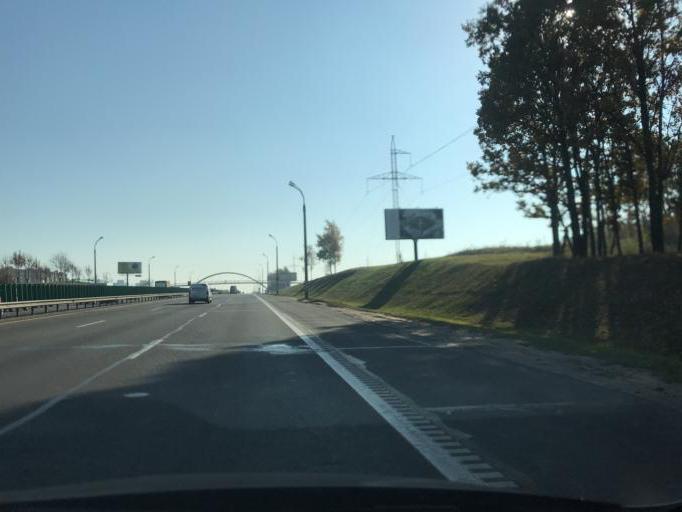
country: BY
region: Minsk
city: Malinovka
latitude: 53.8672
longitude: 27.4239
